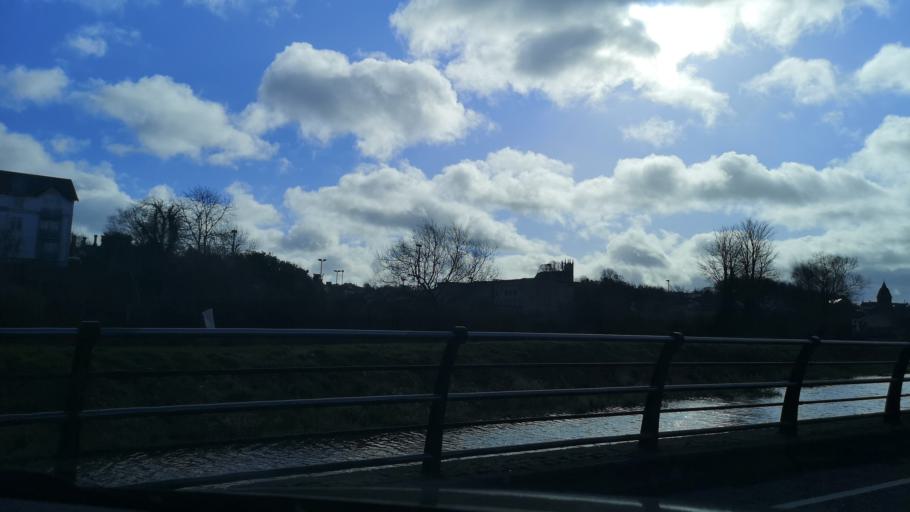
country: GB
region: Northern Ireland
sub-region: Newry and Mourne District
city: Newry
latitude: 54.1817
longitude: -6.3370
